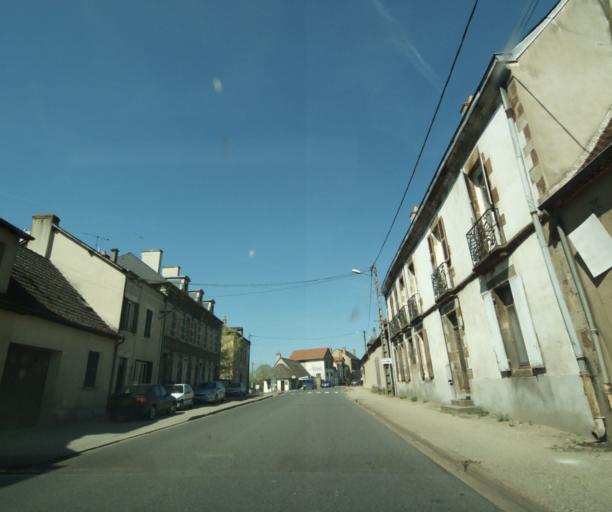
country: FR
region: Auvergne
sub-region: Departement de l'Allier
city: Trevol
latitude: 46.6595
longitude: 3.2484
